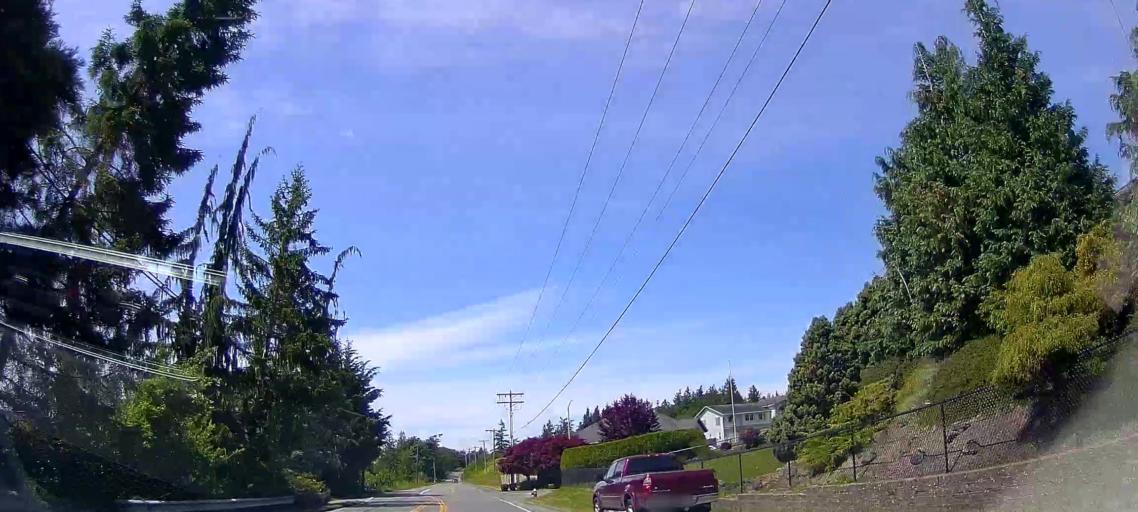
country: US
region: Washington
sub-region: Snohomish County
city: Stanwood
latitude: 48.2501
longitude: -122.3514
